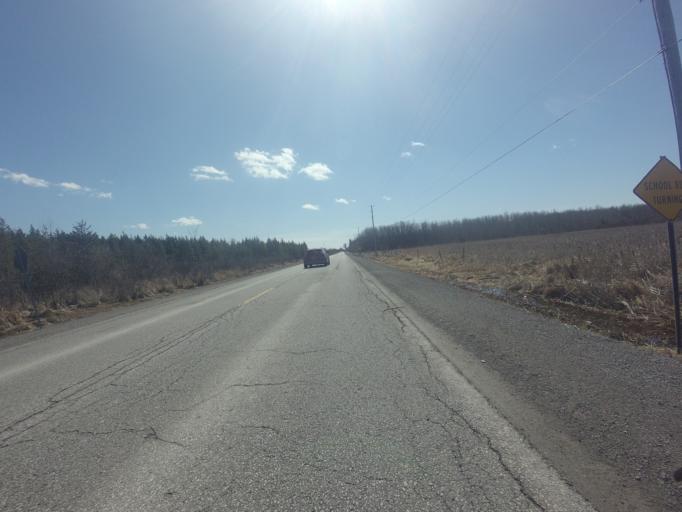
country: CA
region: Ontario
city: Carleton Place
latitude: 45.1656
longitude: -76.0434
